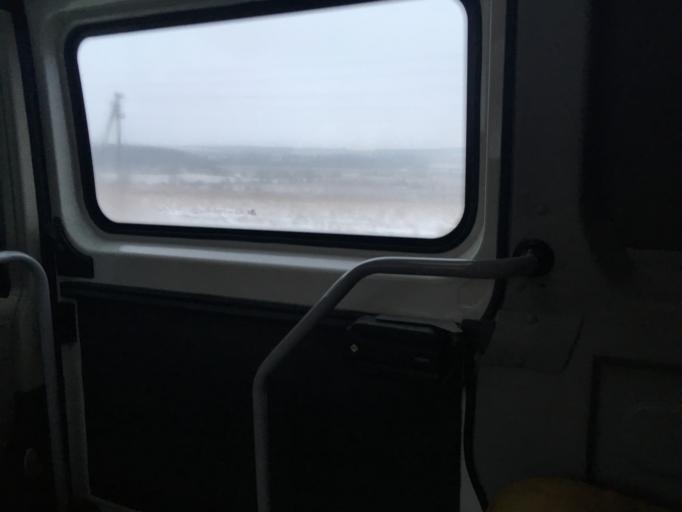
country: RU
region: Tula
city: Dubna
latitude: 54.0901
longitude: 37.0759
